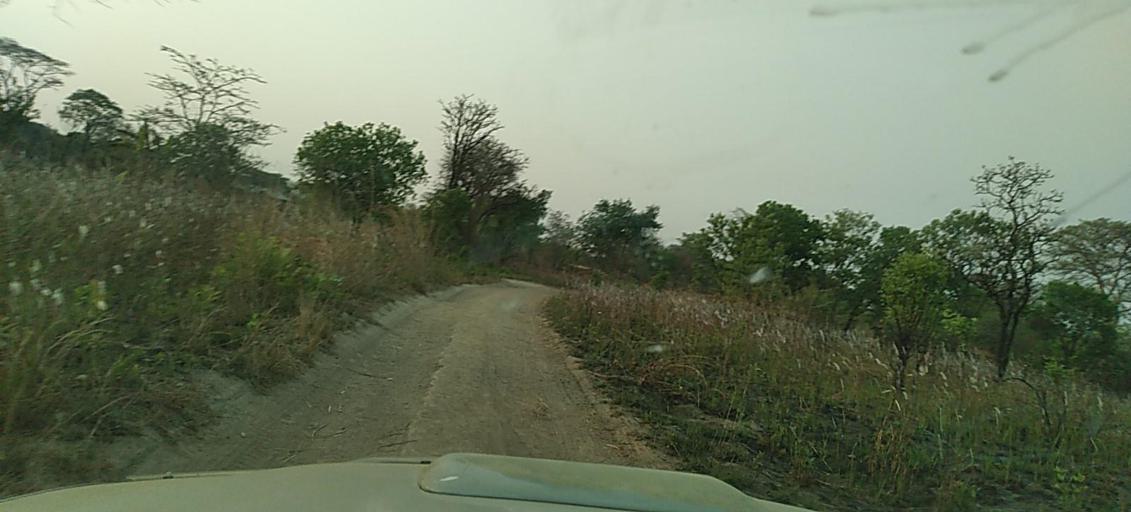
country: ZM
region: North-Western
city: Kasempa
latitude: -13.0690
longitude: 26.3809
